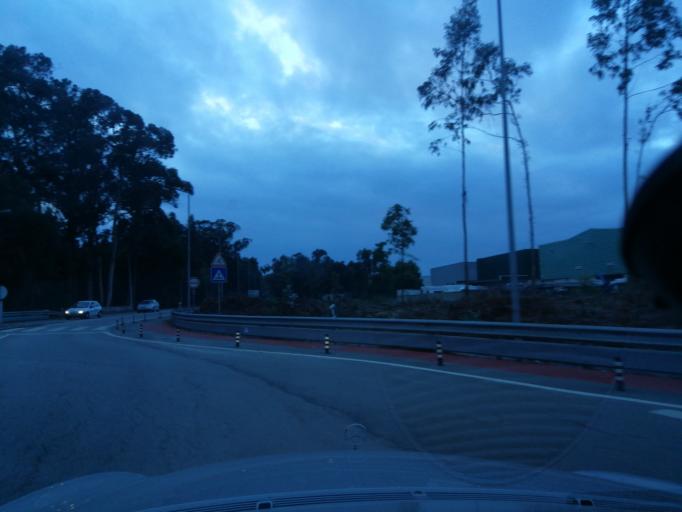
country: PT
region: Aveiro
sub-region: Murtosa
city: Murtosa
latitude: 40.7621
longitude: -8.6330
